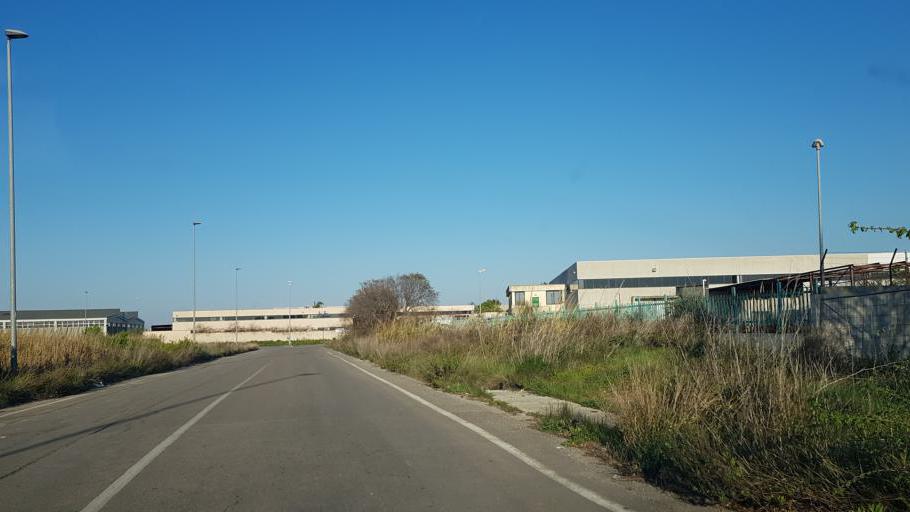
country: IT
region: Apulia
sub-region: Provincia di Brindisi
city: La Rosa
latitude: 40.6274
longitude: 17.9650
